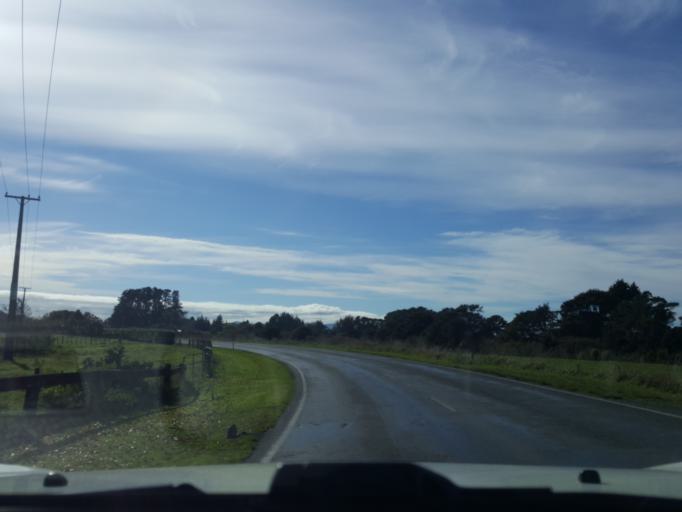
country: NZ
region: Waikato
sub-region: Waikato District
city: Ngaruawahia
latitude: -37.6091
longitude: 175.1967
